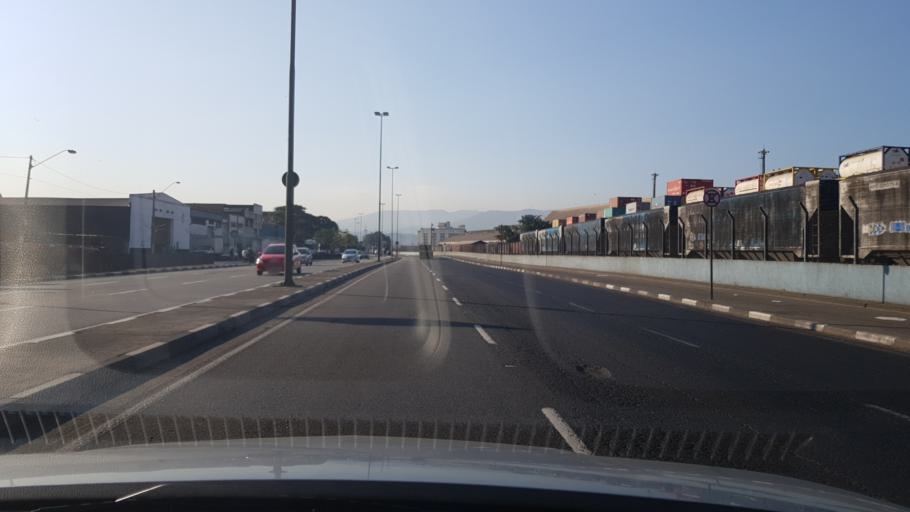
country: BR
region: Sao Paulo
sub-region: Santos
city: Santos
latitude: -23.9480
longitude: -46.3176
